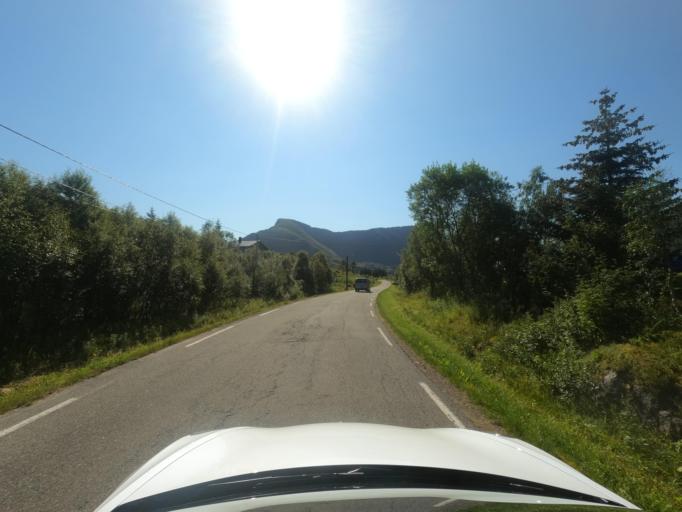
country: NO
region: Nordland
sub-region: Hadsel
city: Stokmarknes
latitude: 68.3076
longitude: 14.9967
